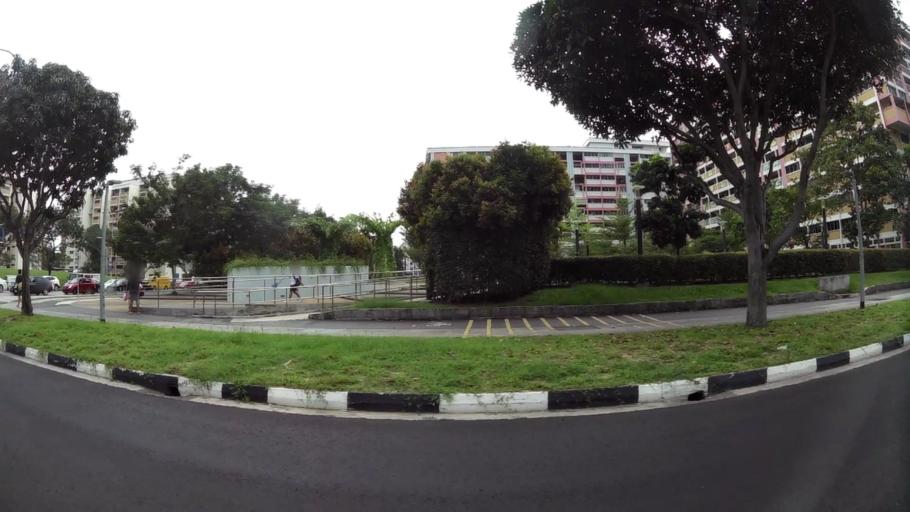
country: SG
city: Singapore
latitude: 1.3518
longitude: 103.9411
